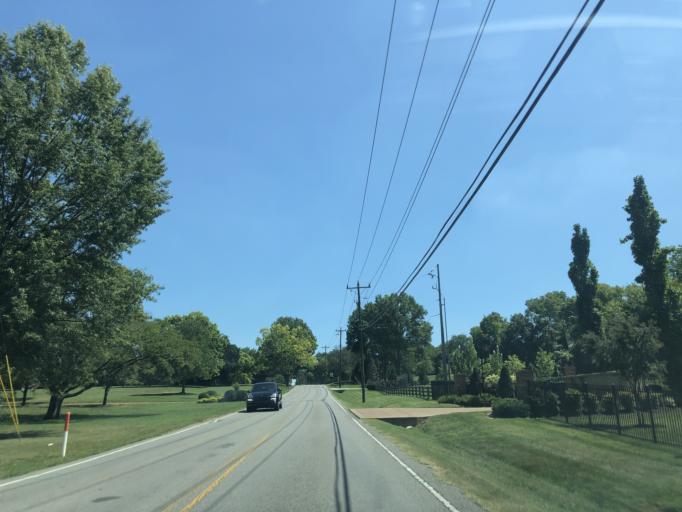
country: US
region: Tennessee
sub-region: Davidson County
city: Oak Hill
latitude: 36.0792
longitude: -86.7891
